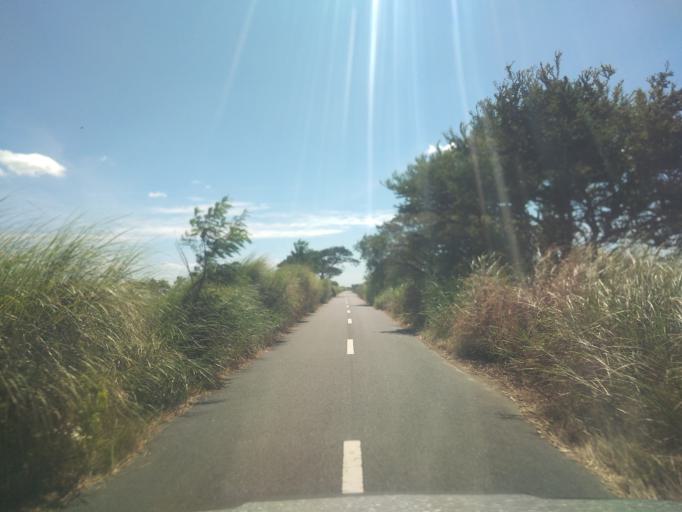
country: PH
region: Central Luzon
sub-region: Province of Pampanga
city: San Basilio
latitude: 15.0340
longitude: 120.5970
